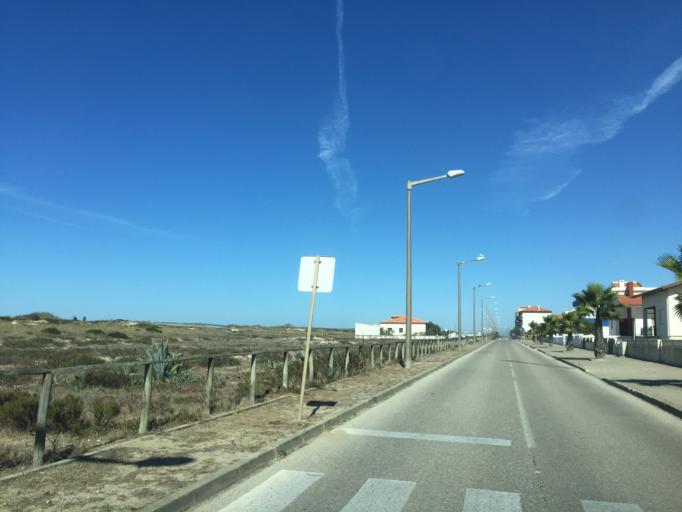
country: PT
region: Coimbra
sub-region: Figueira da Foz
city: Buarcos
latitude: 40.2139
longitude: -8.8939
